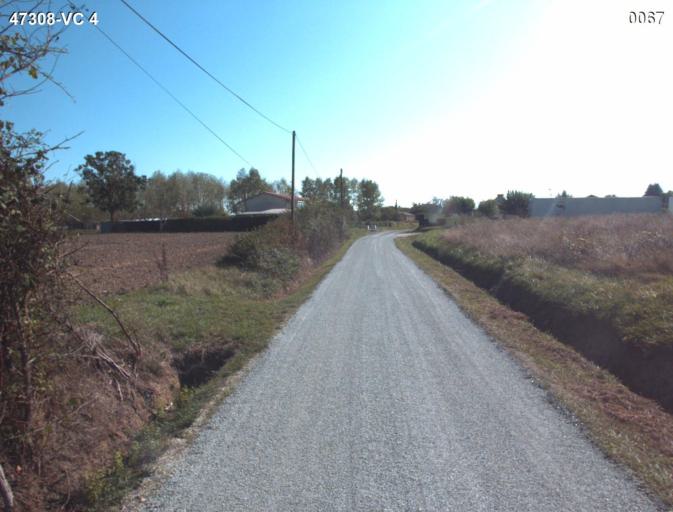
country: FR
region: Aquitaine
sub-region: Departement du Lot-et-Garonne
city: Buzet-sur-Baise
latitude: 44.2557
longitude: 0.3341
